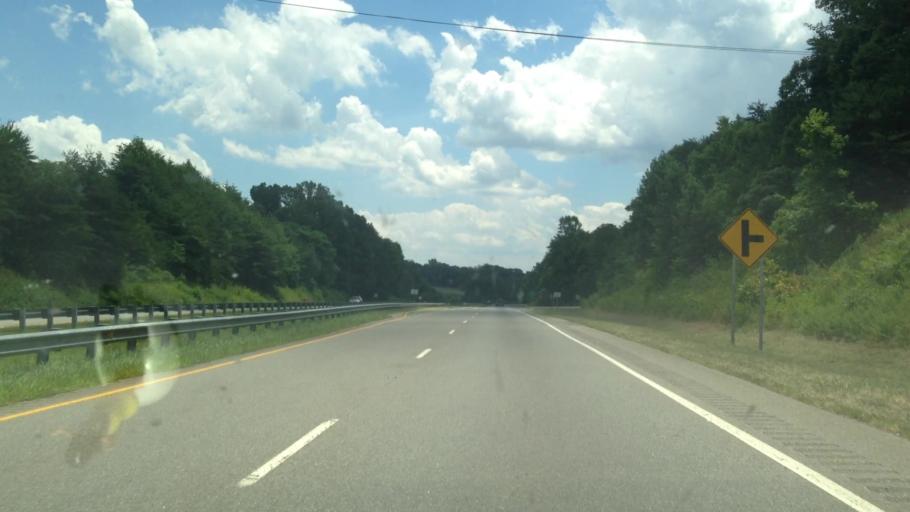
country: US
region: North Carolina
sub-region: Rockingham County
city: Stoneville
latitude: 36.5217
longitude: -79.9178
